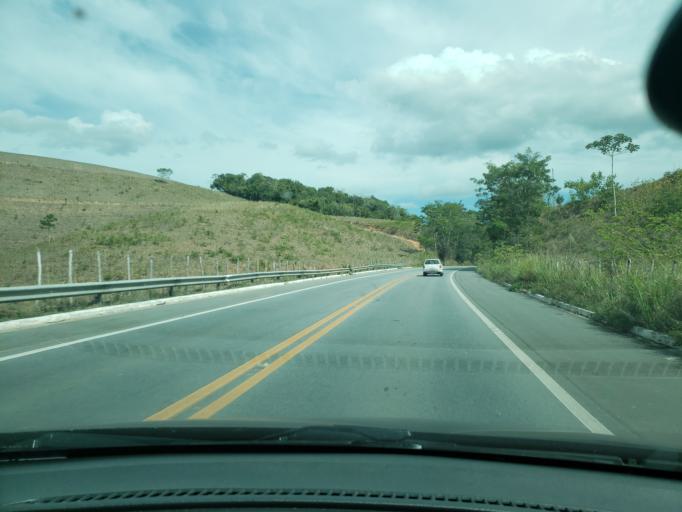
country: BR
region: Alagoas
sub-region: Murici
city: Murici
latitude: -9.3285
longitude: -35.9179
